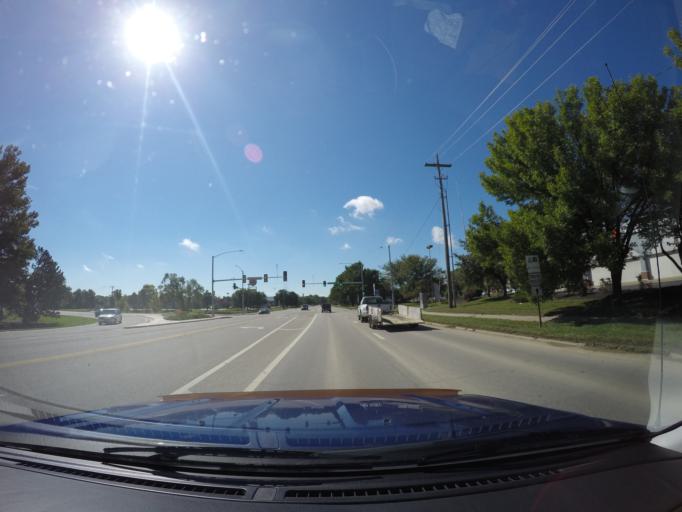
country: US
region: Kansas
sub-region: Douglas County
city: Lawrence
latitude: 38.9919
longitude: -95.2335
